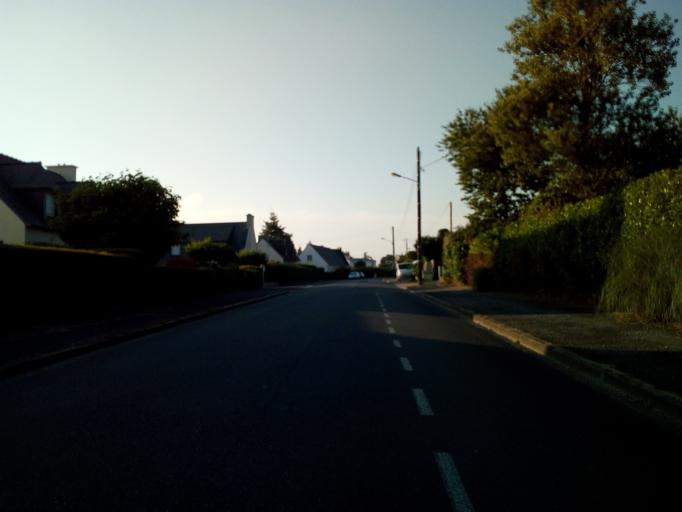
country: FR
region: Brittany
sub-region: Departement du Finistere
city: Landivisiau
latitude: 48.5000
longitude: -4.0786
